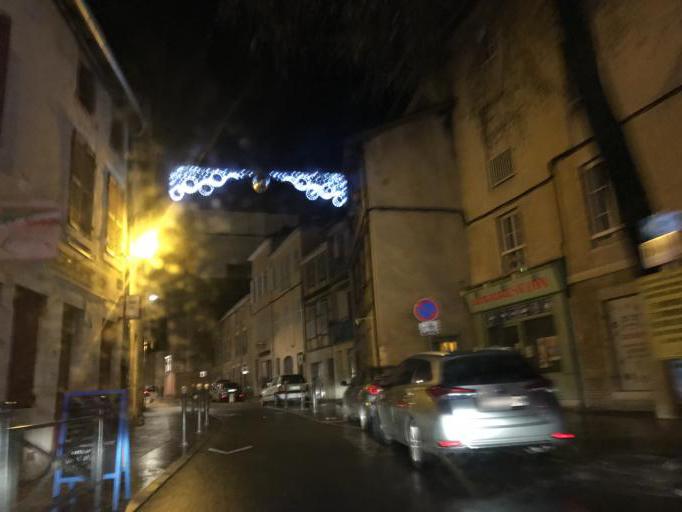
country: FR
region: Rhone-Alpes
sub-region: Departement de l'Ain
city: Bourg-en-Bresse
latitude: 46.2033
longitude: 5.2263
